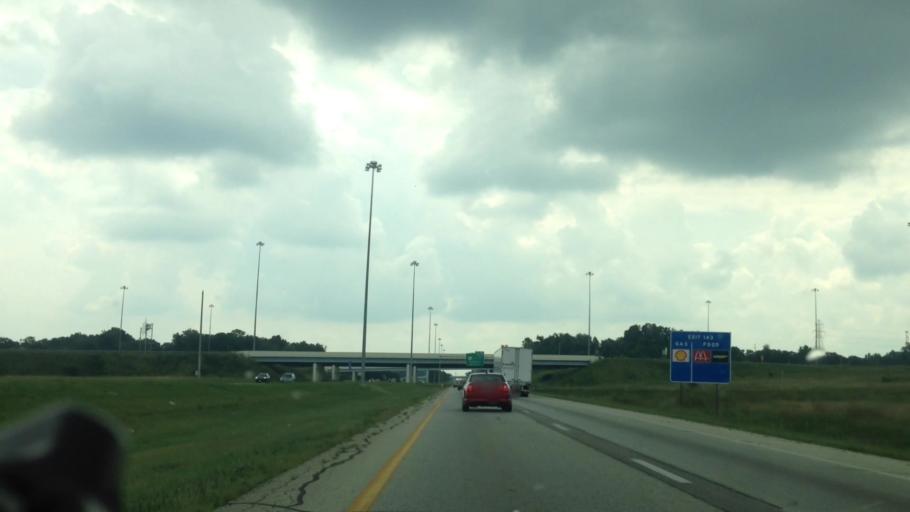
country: US
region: Ohio
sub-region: Summit County
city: Richfield
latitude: 41.2316
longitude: -81.6278
